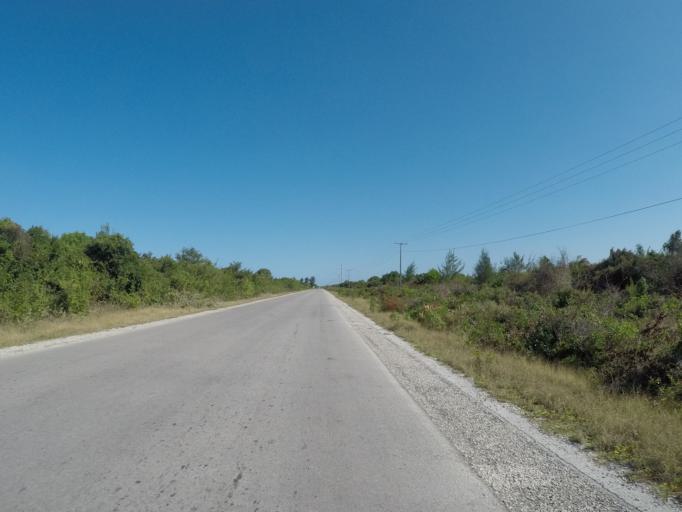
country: TZ
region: Zanzibar Central/South
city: Nganane
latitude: -6.1710
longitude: 39.5263
